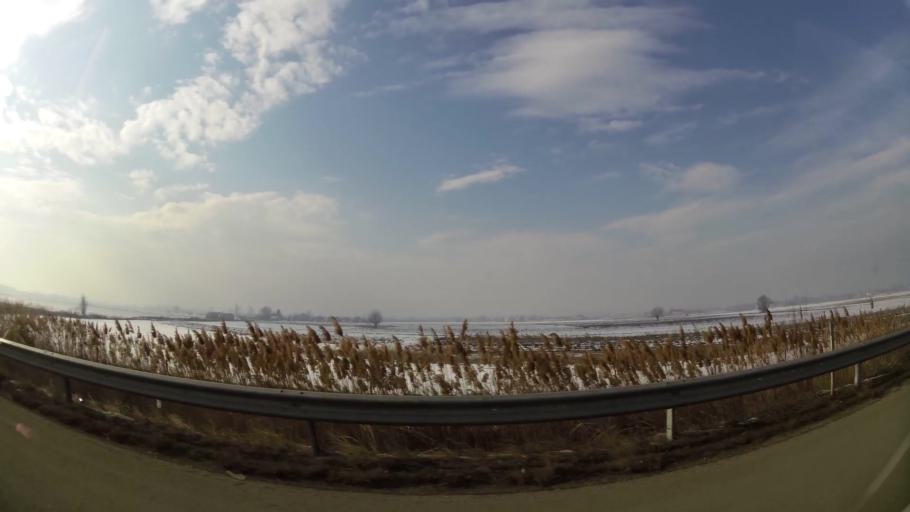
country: MK
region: Aracinovo
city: Arachinovo
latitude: 42.0025
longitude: 21.5339
